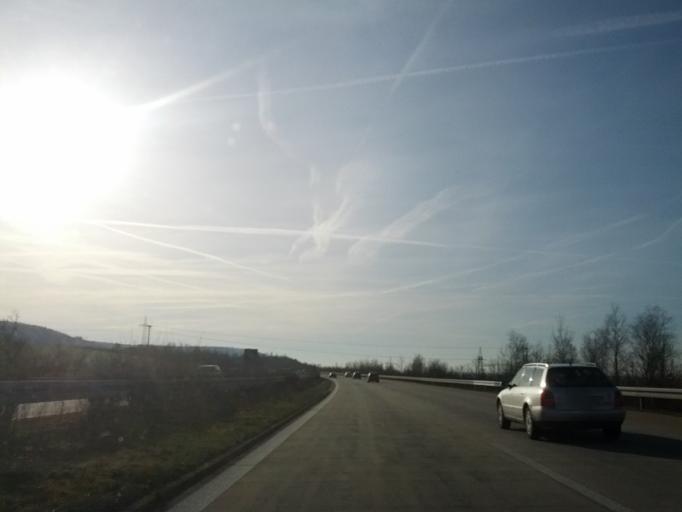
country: DE
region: Bavaria
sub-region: Regierungsbezirk Mittelfranken
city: Steinsfeld
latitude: 49.4180
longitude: 10.2497
